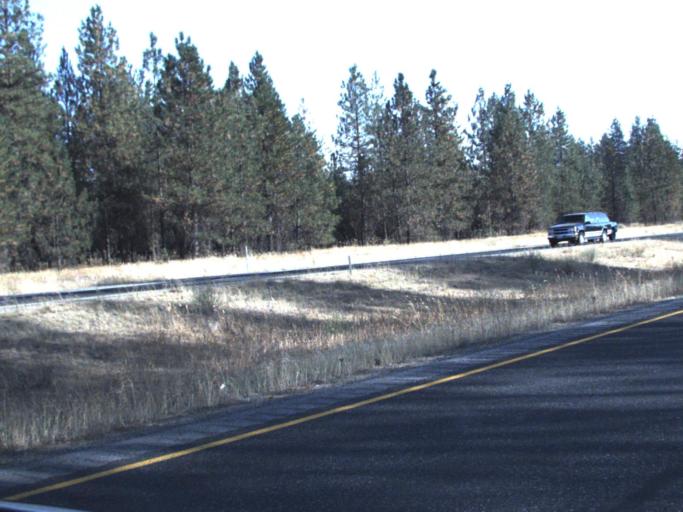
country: US
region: Washington
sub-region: Spokane County
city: Mead
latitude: 47.8492
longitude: -117.3551
